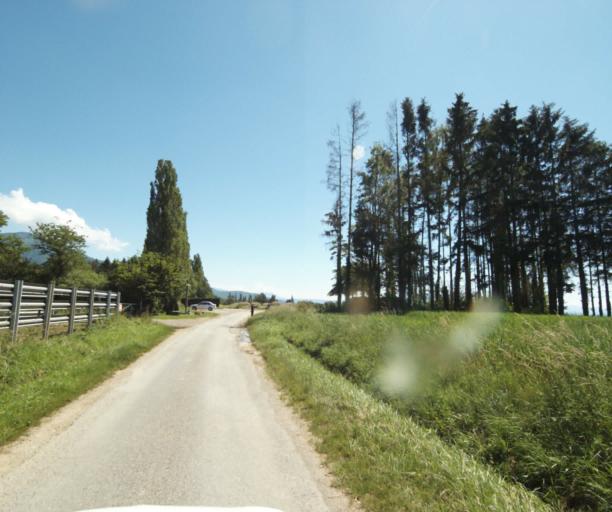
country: FR
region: Rhone-Alpes
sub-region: Departement de la Haute-Savoie
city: Loisin
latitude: 46.2820
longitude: 6.3250
